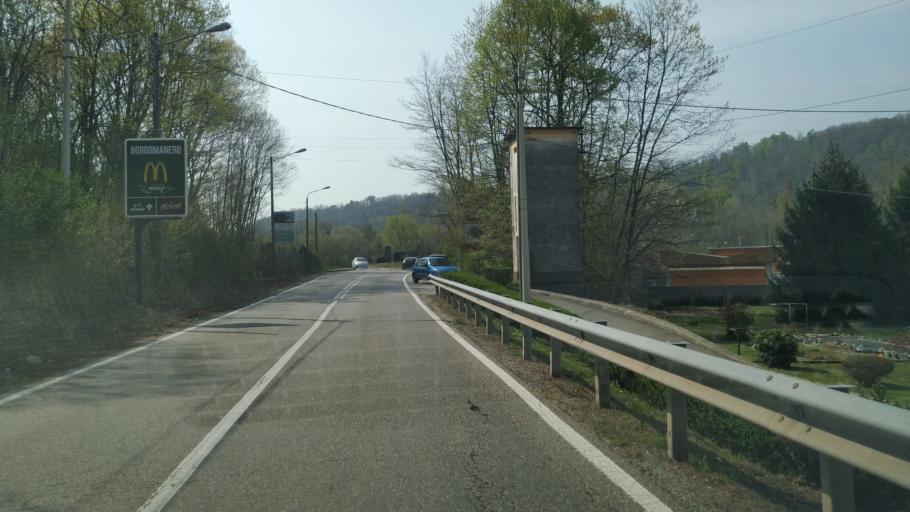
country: IT
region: Piedmont
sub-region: Provincia di Novara
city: Soriso
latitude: 45.7568
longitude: 8.4199
